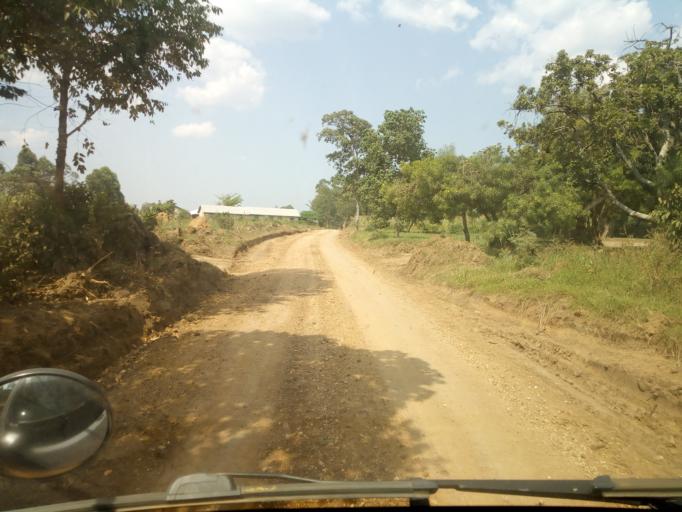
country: UG
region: Western Region
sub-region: Kanungu District
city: Ntungamo
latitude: -0.7834
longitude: 29.6960
